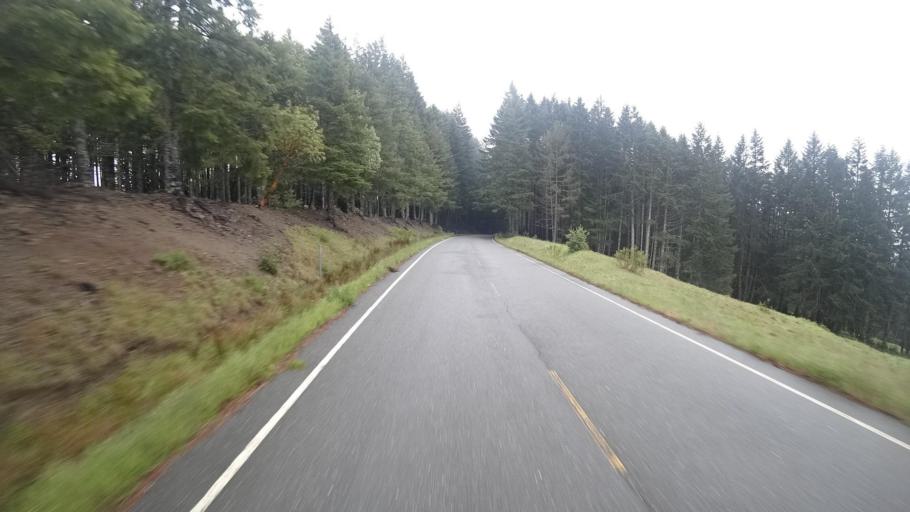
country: US
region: California
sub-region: Humboldt County
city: Westhaven-Moonstone
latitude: 41.2034
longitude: -123.9468
